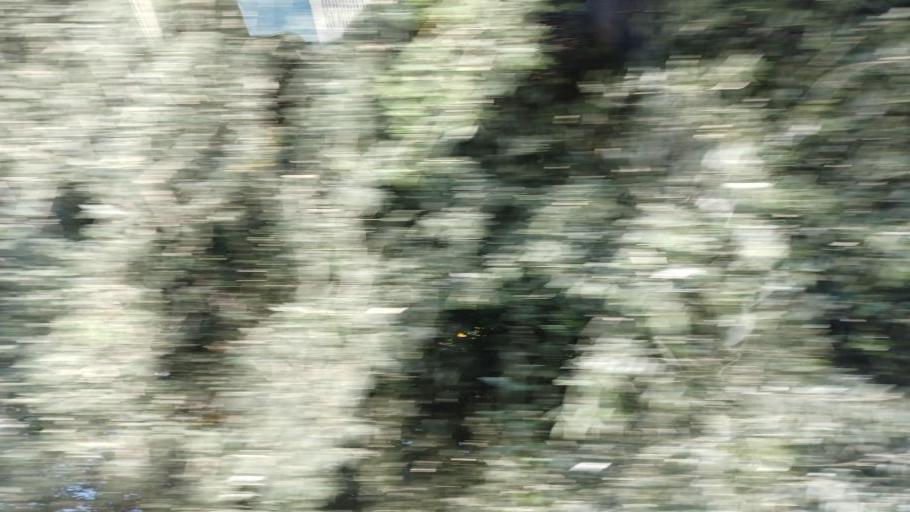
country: CY
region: Pafos
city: Pegeia
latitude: 34.8592
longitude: 32.3822
